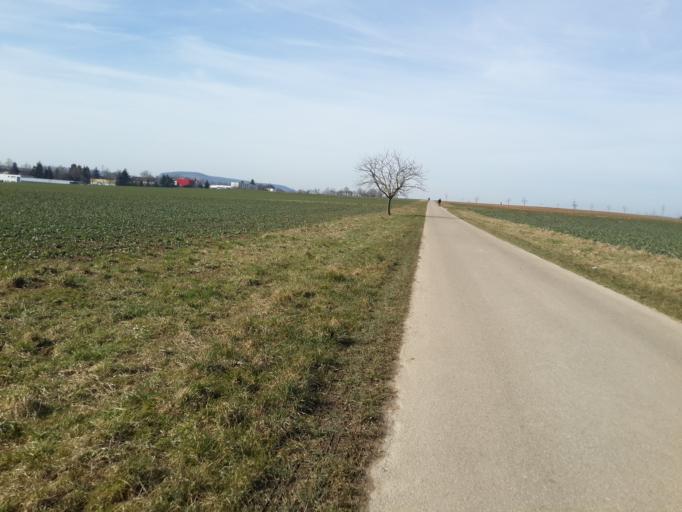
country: DE
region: Baden-Wuerttemberg
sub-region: Regierungsbezirk Stuttgart
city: Heilbronn
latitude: 49.1459
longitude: 9.1727
